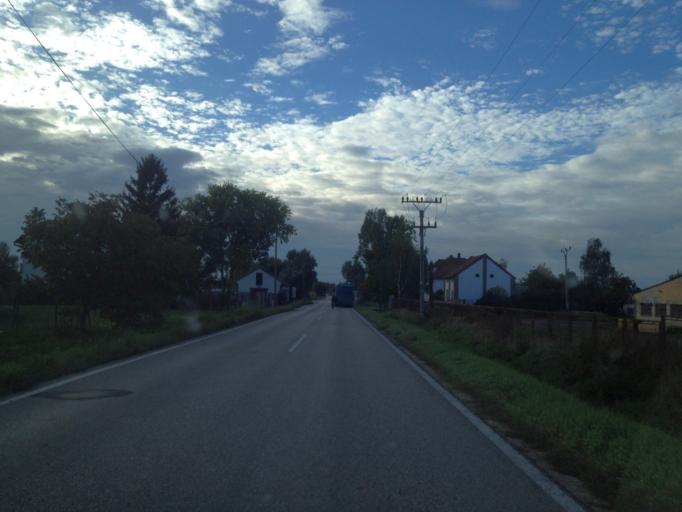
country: HU
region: Komarom-Esztergom
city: Almasfuzito
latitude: 47.7460
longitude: 18.2384
